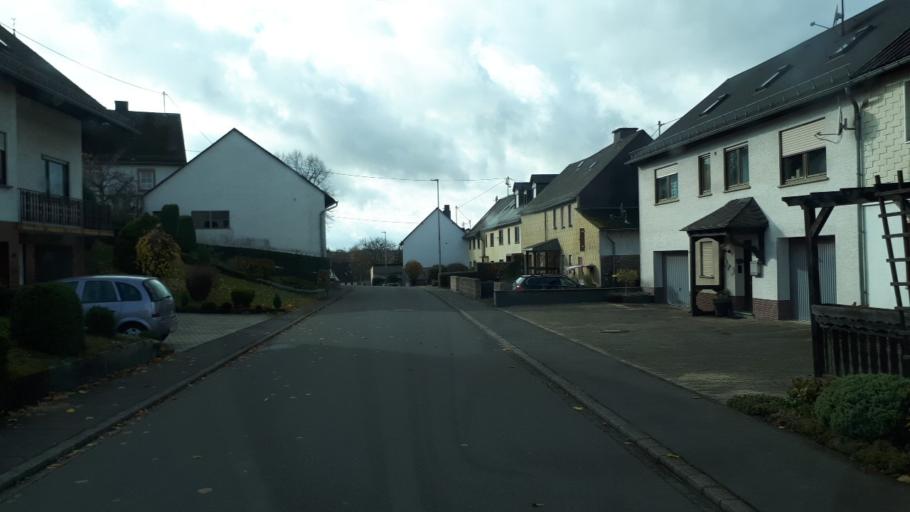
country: DE
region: Rheinland-Pfalz
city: Alflen
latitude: 50.1766
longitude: 7.0431
